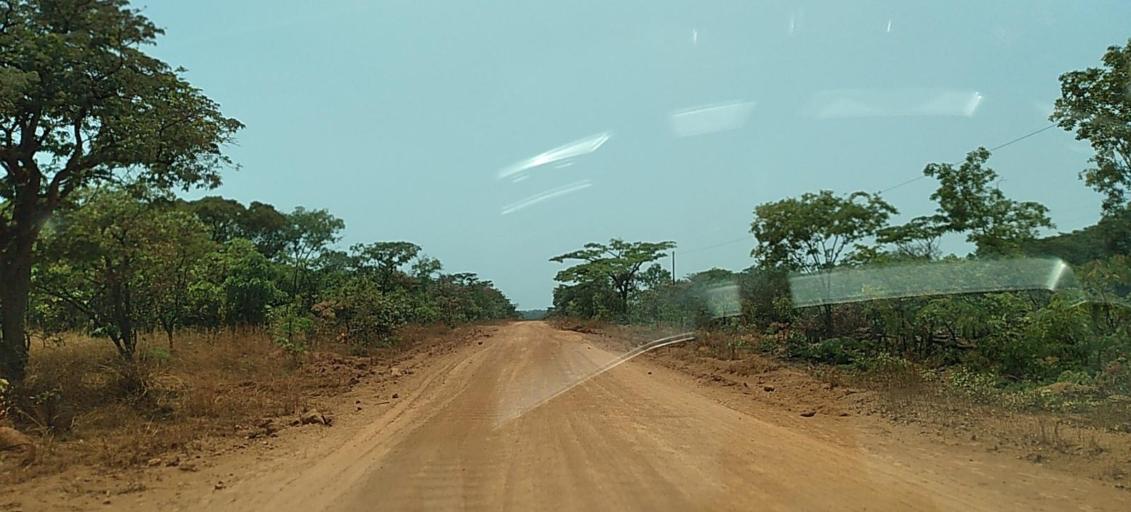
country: CD
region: Katanga
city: Kipushi
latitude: -11.9262
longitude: 27.0007
